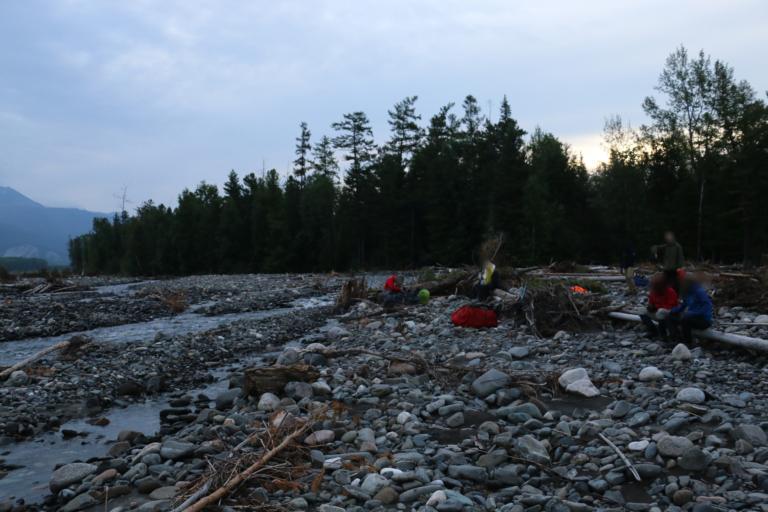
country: RU
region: Respublika Buryatiya
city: Novyy Uoyan
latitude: 56.1873
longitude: 111.5105
